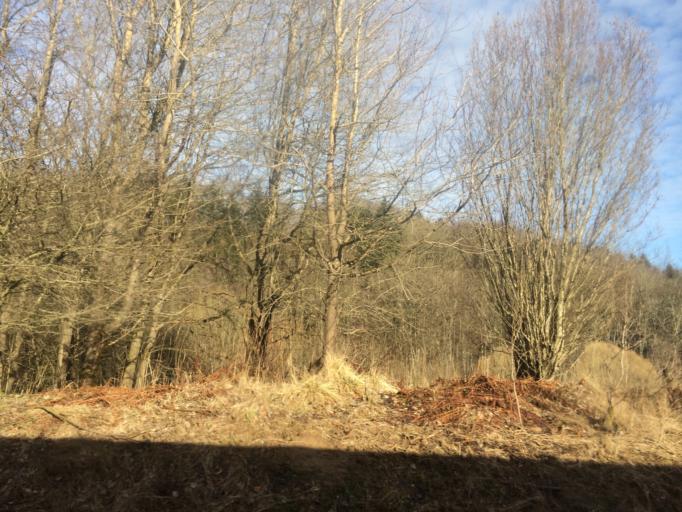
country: DK
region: South Denmark
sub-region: Vejle Kommune
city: Vejle
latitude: 55.7612
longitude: 9.4943
